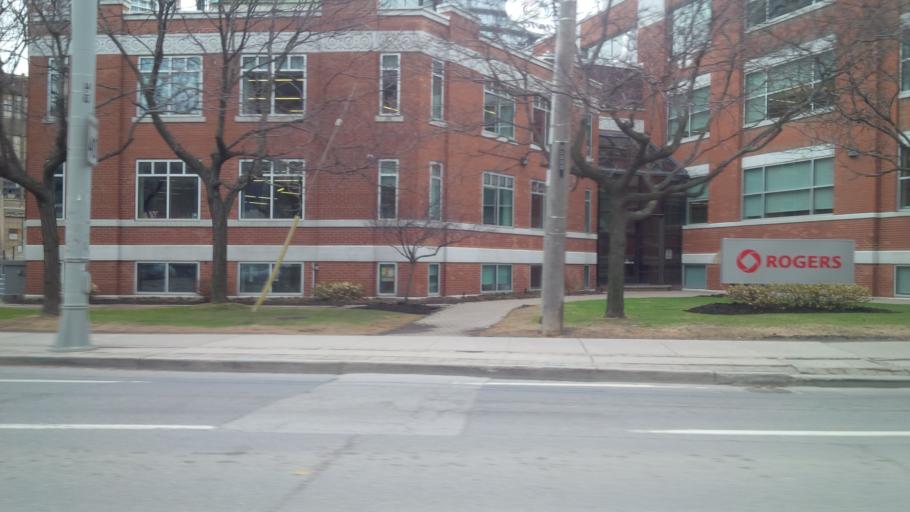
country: CA
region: Ontario
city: Toronto
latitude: 43.6362
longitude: -79.3994
